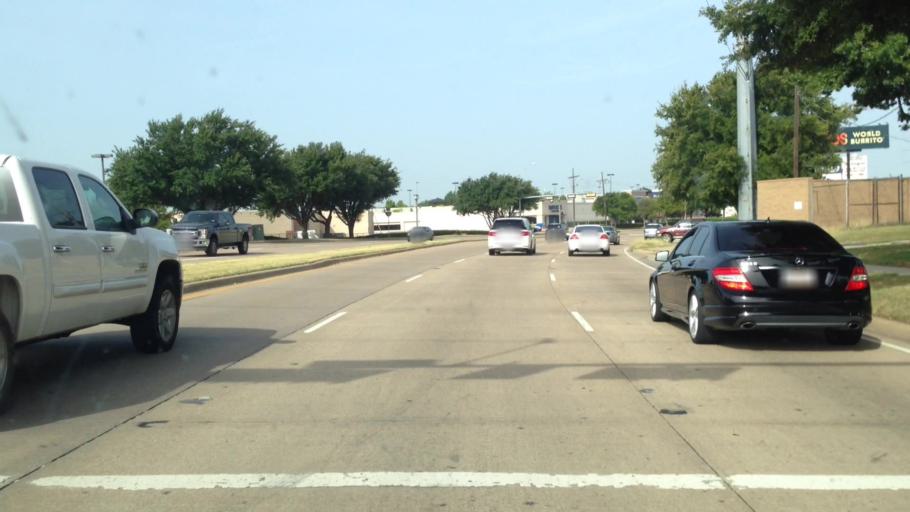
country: US
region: Texas
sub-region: Denton County
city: Lewisville
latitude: 33.0053
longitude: -96.9740
